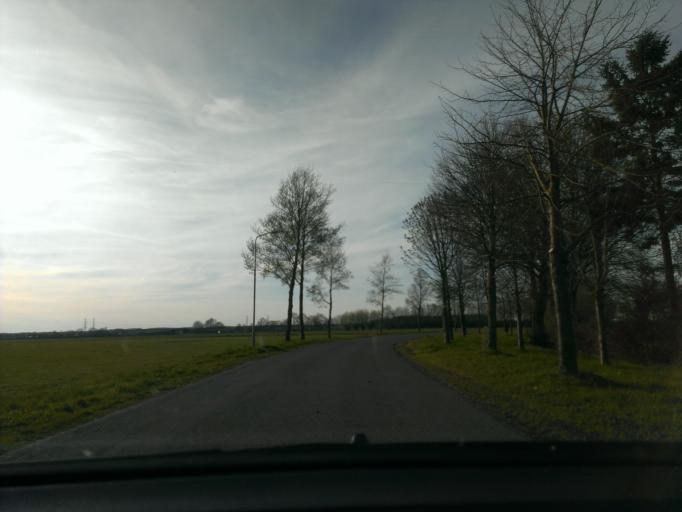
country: NL
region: Overijssel
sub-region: Gemeente Olst-Wijhe
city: Wijhe
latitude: 52.3910
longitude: 6.0985
